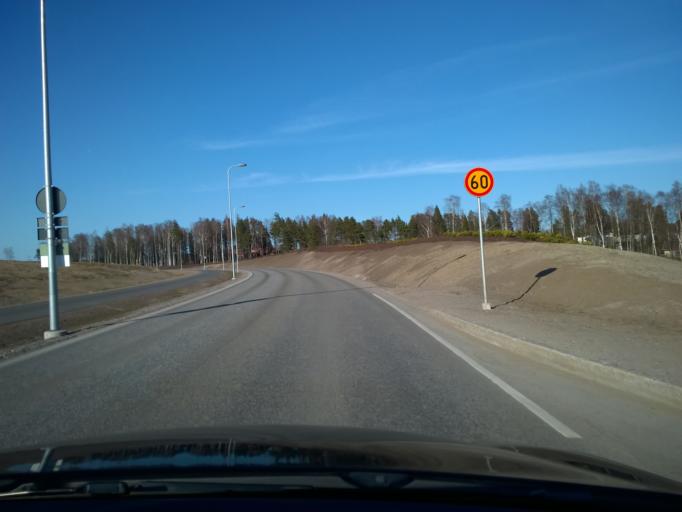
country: FI
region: Uusimaa
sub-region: Helsinki
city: Kilo
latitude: 60.1925
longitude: 24.7885
